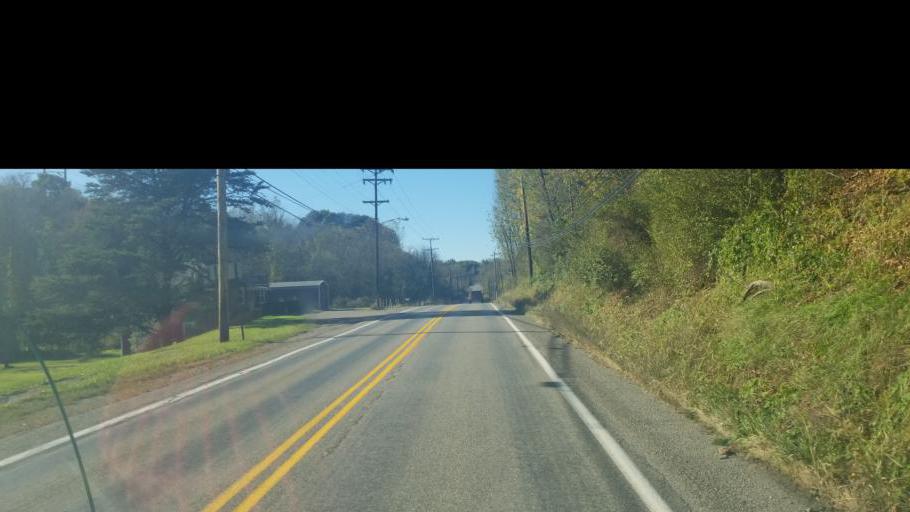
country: US
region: Pennsylvania
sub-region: Allegheny County
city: Imperial
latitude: 40.4636
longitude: -80.2688
